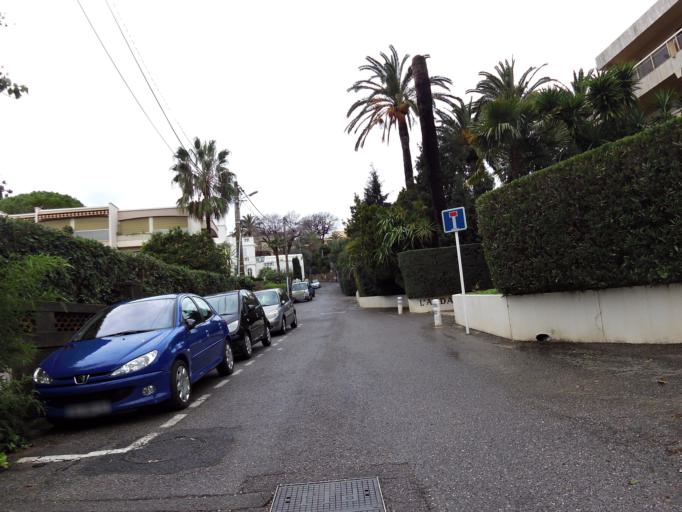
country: FR
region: Provence-Alpes-Cote d'Azur
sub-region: Departement des Alpes-Maritimes
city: Antibes
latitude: 43.5727
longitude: 7.1213
